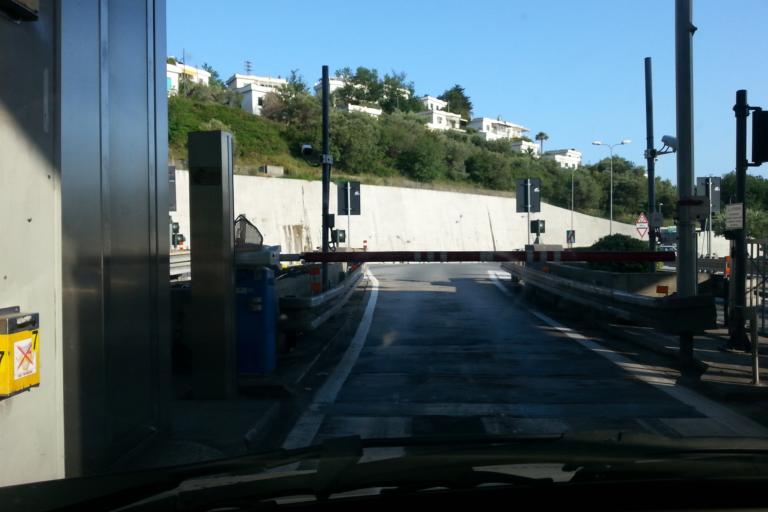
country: IT
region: Liguria
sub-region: Provincia di Savona
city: Pietra Ligure
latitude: 44.1552
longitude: 8.2709
